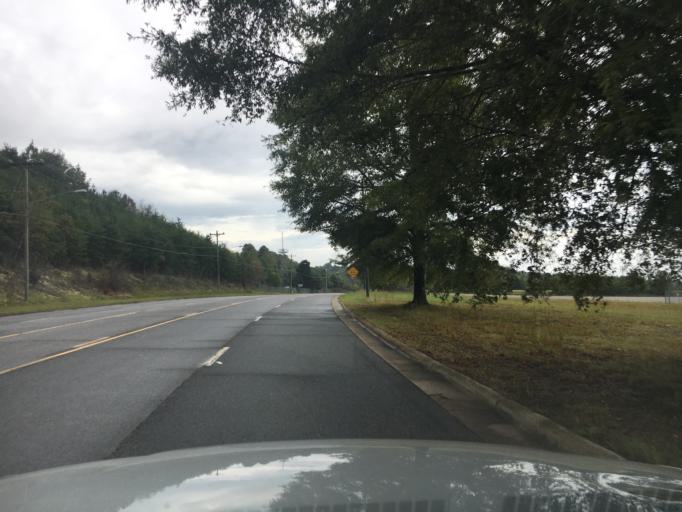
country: US
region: North Carolina
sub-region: Catawba County
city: Longview
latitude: 35.7473
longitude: -81.3739
